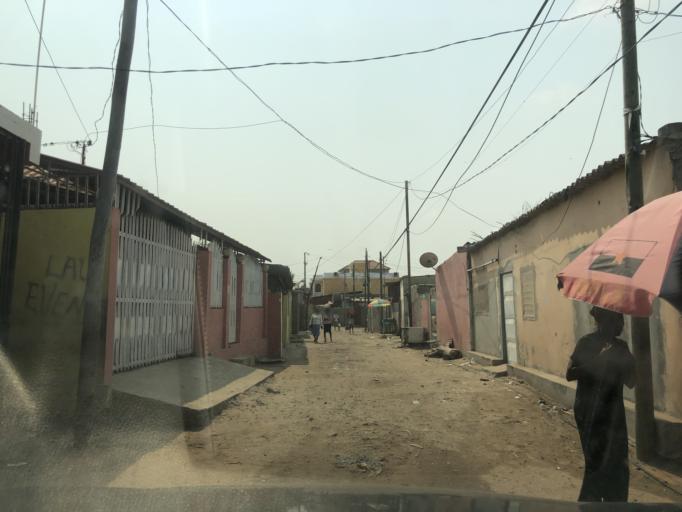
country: AO
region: Luanda
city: Luanda
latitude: -8.9034
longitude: 13.1656
